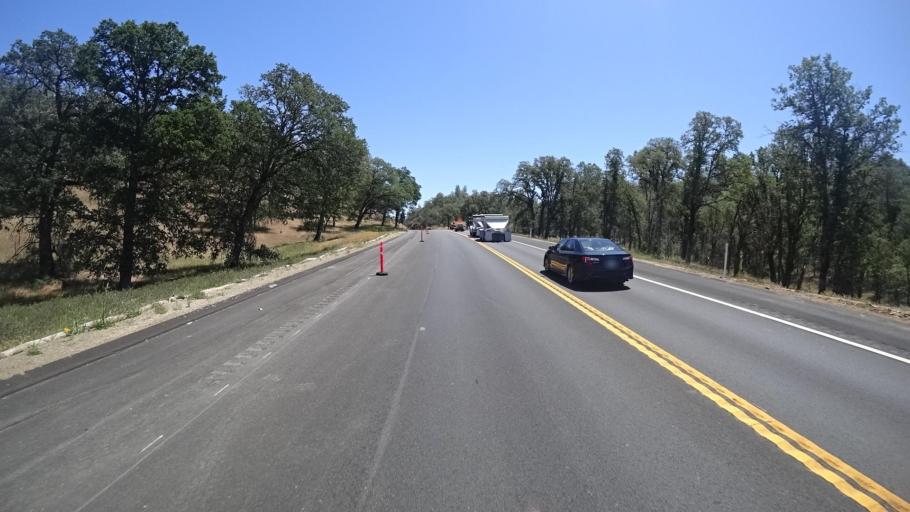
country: US
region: California
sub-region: Lake County
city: Hidden Valley Lake
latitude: 38.8422
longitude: -122.6048
